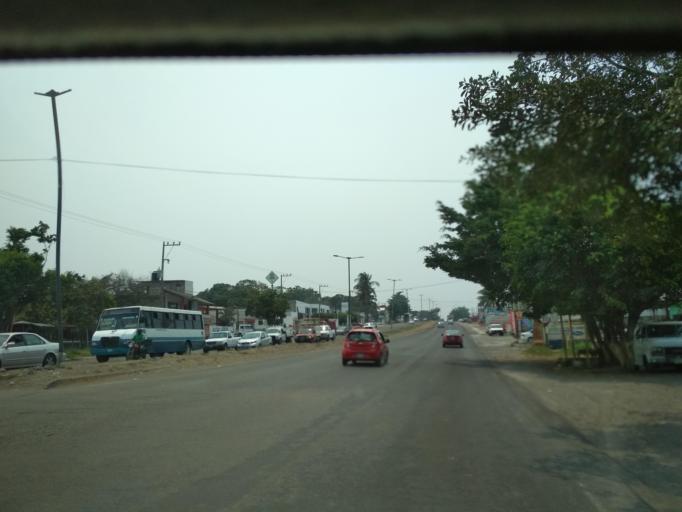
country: MX
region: Veracruz
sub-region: Veracruz
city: Las Amapolas
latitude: 19.1646
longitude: -96.2127
